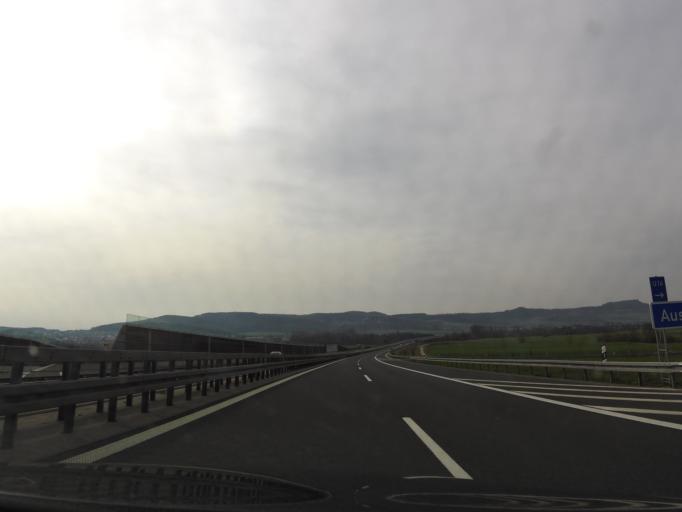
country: DE
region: Bavaria
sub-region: Upper Franconia
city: Lichtenfels
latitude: 50.1487
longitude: 11.0300
